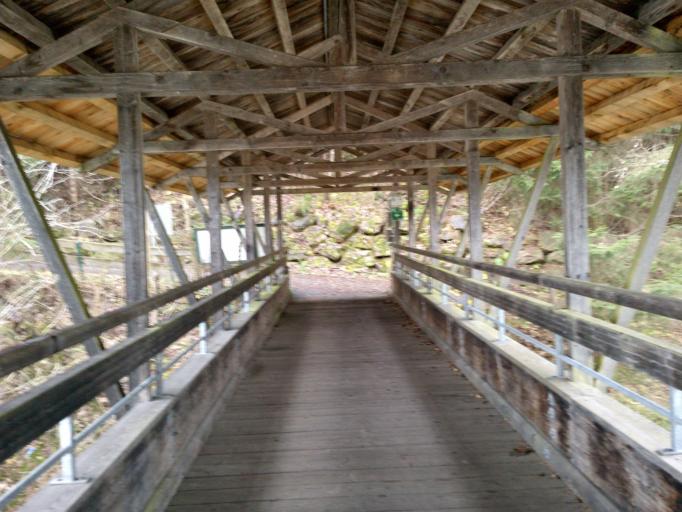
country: AT
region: Styria
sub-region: Politischer Bezirk Murtal
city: Judenburg
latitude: 47.1727
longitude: 14.6484
